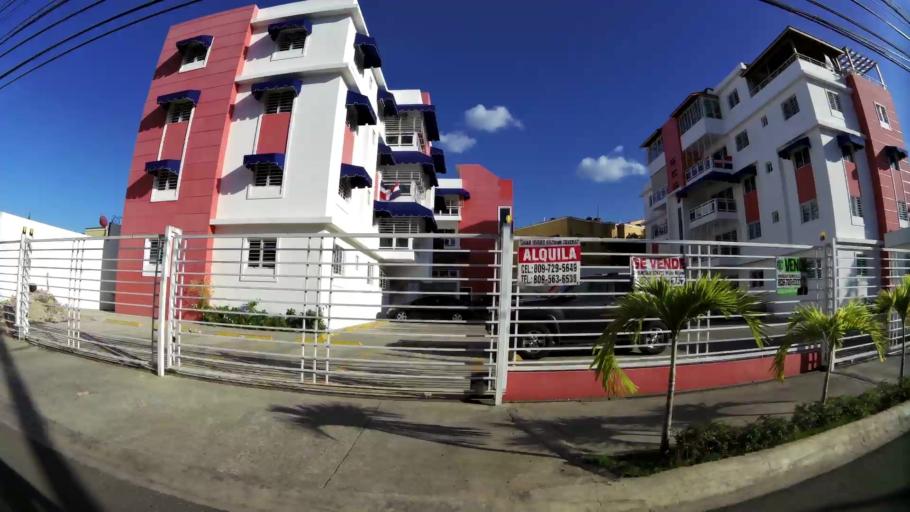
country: DO
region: Nacional
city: Santo Domingo
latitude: 18.4949
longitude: -69.9722
